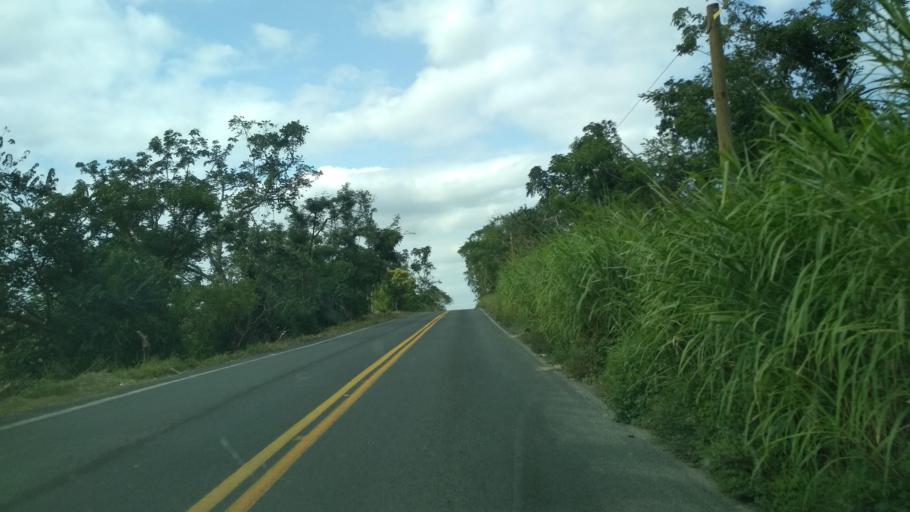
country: MX
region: Veracruz
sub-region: Papantla
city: Polutla
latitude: 20.4597
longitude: -97.2511
